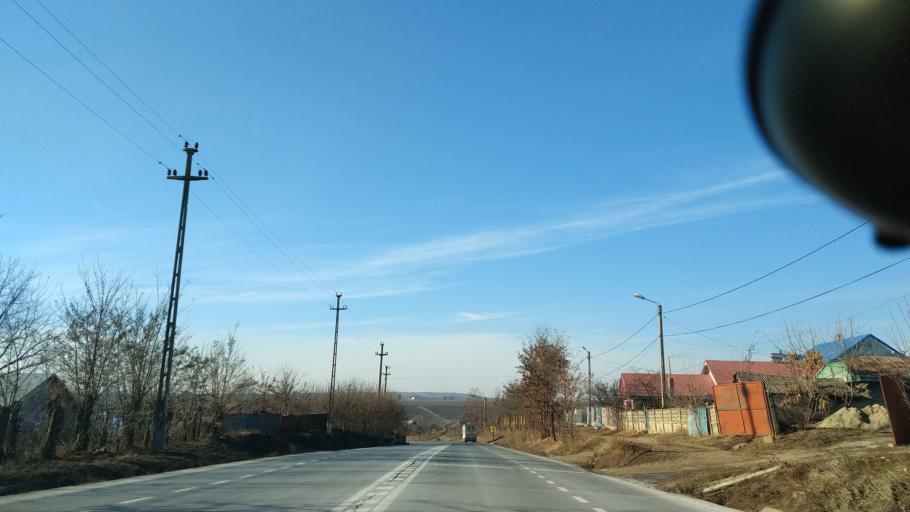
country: RO
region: Iasi
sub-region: Comuna Lungani
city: Zmeu
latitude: 47.2252
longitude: 27.1845
